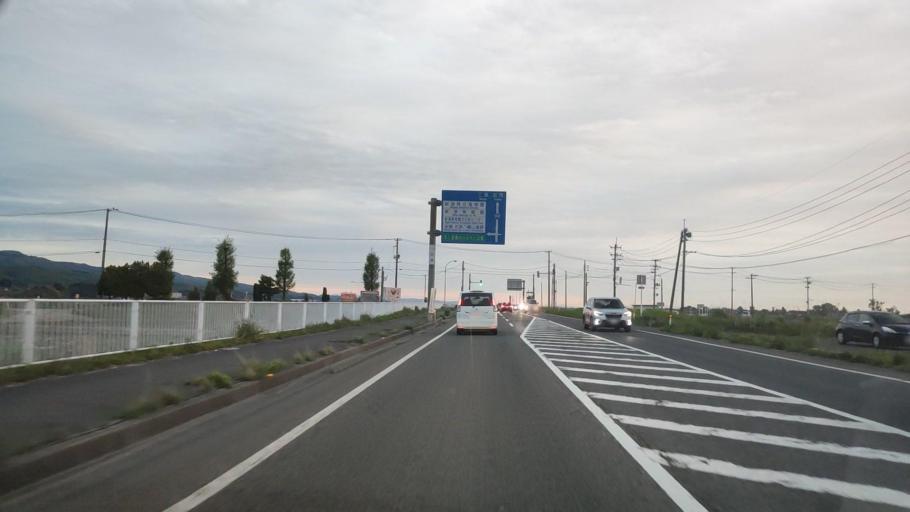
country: JP
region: Niigata
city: Niitsu-honcho
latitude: 37.7721
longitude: 139.1036
